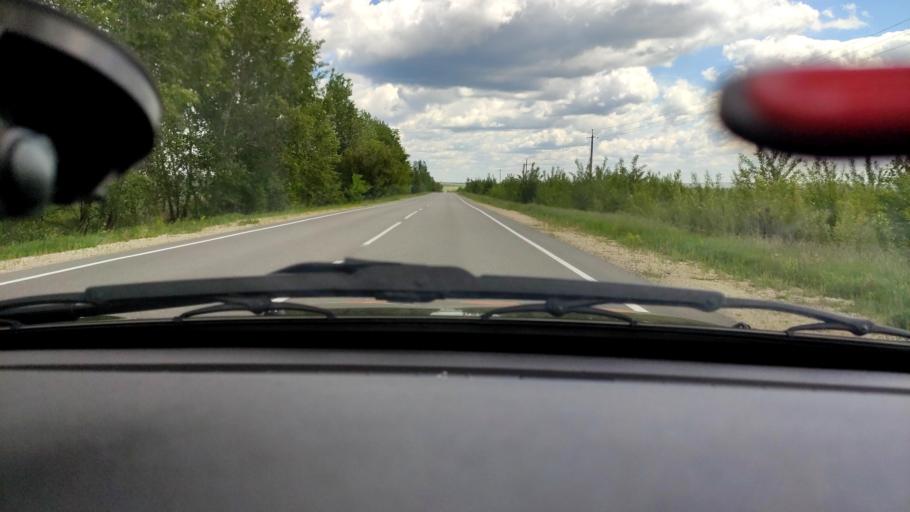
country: RU
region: Belgorod
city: Krasnoye
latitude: 51.0684
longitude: 38.7924
